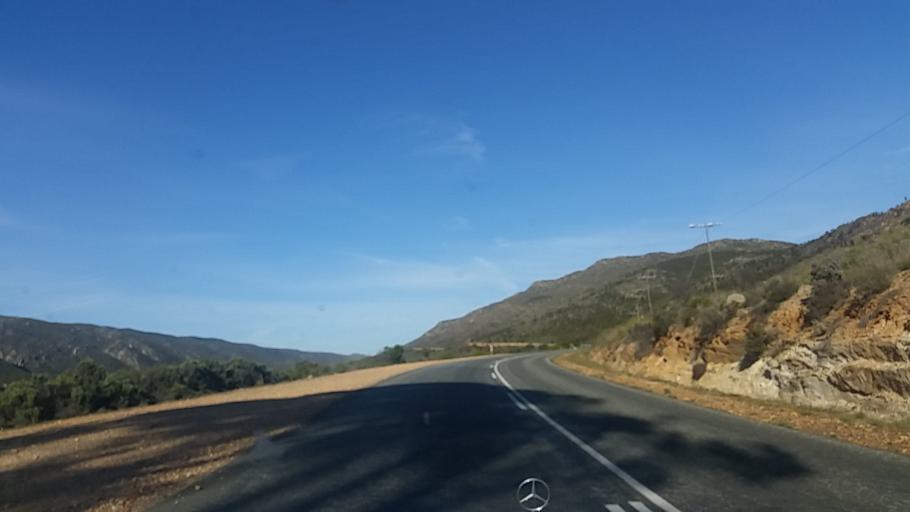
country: ZA
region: Western Cape
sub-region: Eden District Municipality
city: Knysna
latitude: -33.7520
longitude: 22.9516
